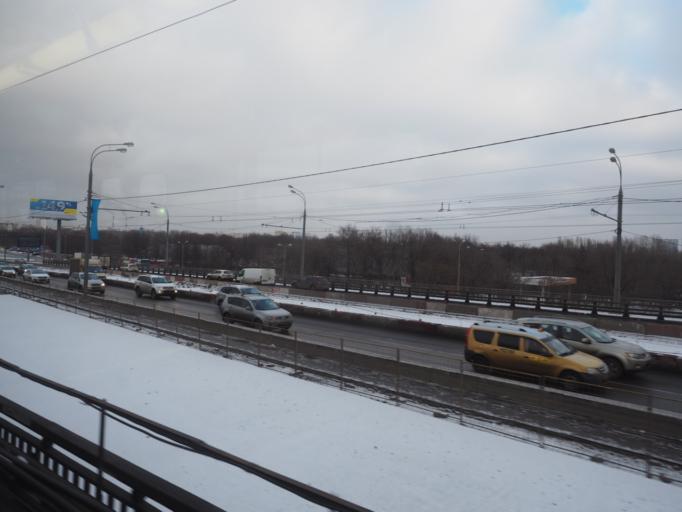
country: RU
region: Moskovskaya
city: Kozhukhovo
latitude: 55.6889
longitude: 37.6652
